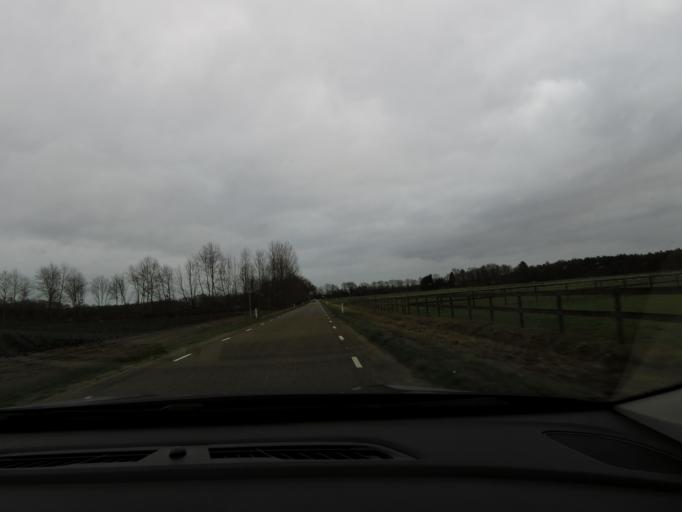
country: NL
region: North Brabant
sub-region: Gemeente Heusden
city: Heusden
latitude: 51.6608
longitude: 5.1568
